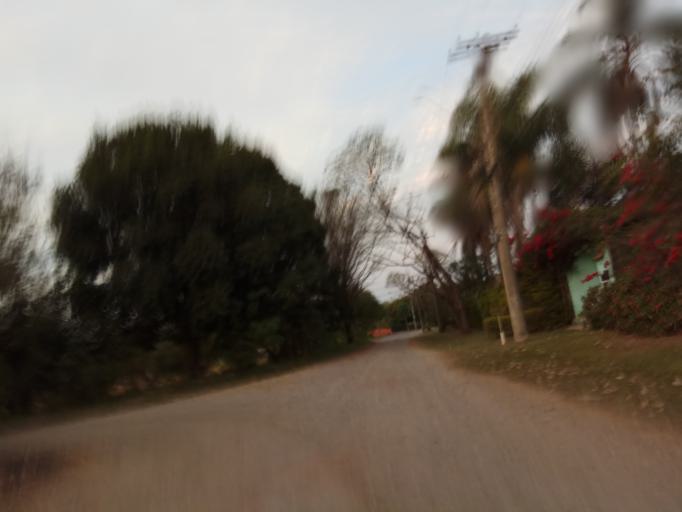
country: BR
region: Sao Paulo
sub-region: Piracicaba
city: Piracicaba
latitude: -22.7562
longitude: -47.5956
